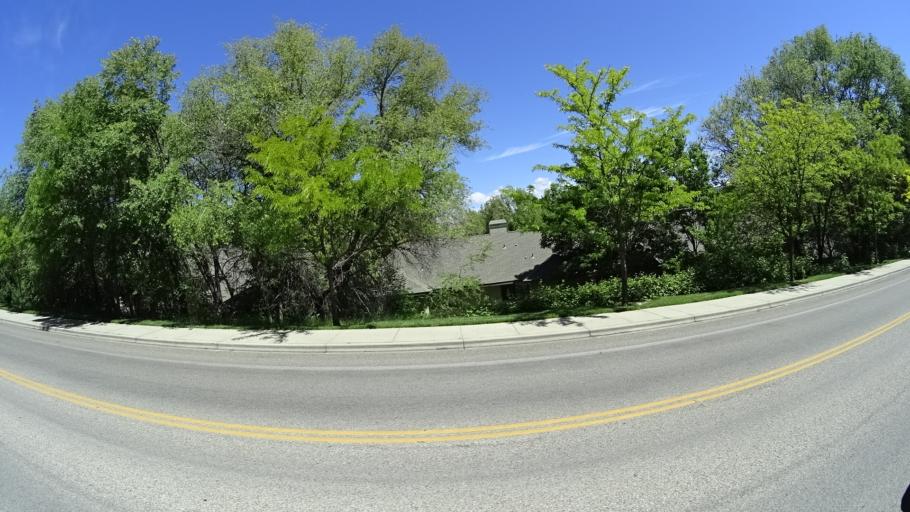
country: US
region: Idaho
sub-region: Ada County
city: Boise
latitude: 43.5680
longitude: -116.1800
